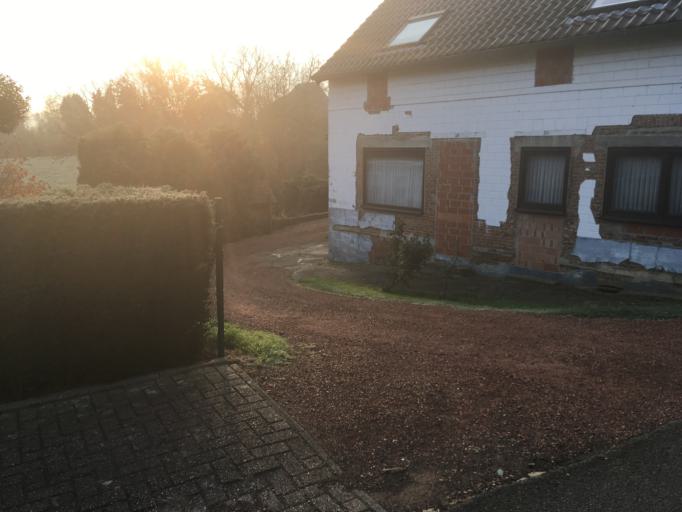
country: BE
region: Flanders
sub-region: Provincie Vlaams-Brabant
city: Beersel
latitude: 50.7273
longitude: 4.3072
